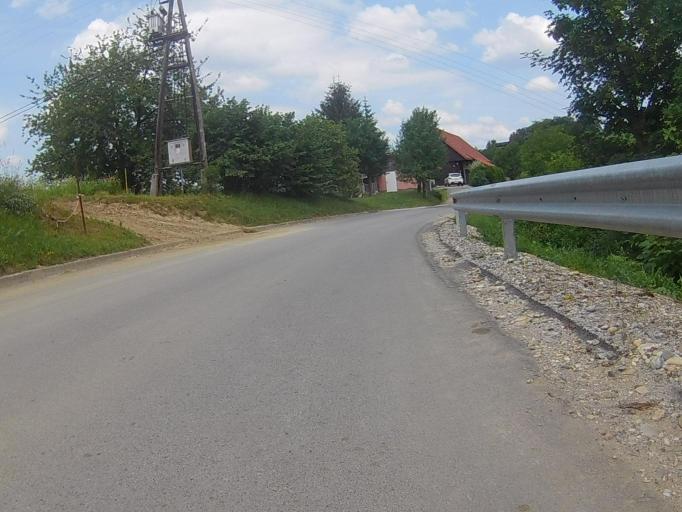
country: SI
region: Kungota
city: Zgornja Kungota
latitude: 46.6579
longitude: 15.6335
